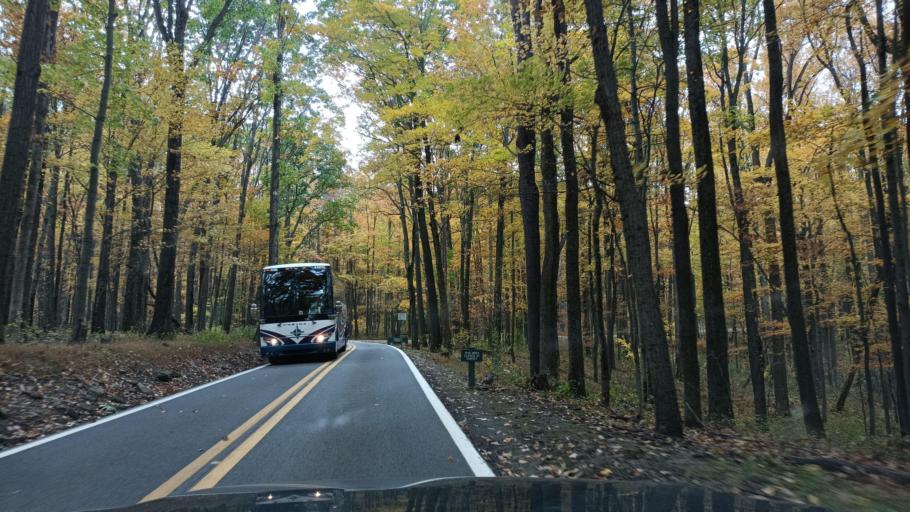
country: US
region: West Virginia
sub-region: Monongalia County
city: Cheat Lake
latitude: 39.6548
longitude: -79.7862
